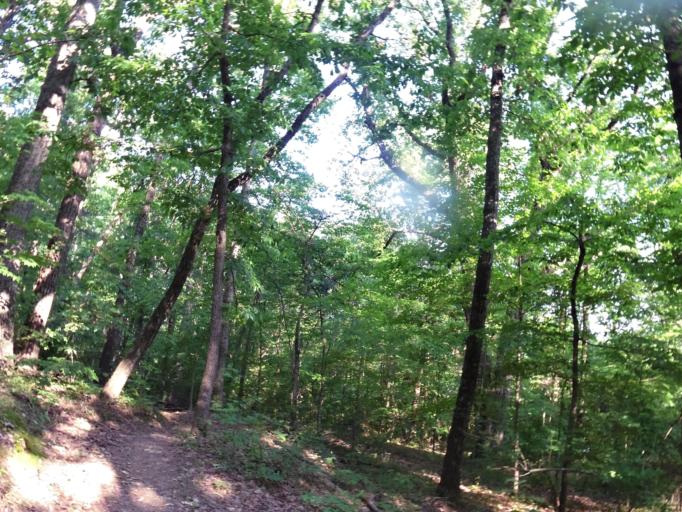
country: US
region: Tennessee
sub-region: Knox County
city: Knoxville
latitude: 36.0042
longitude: -83.9382
